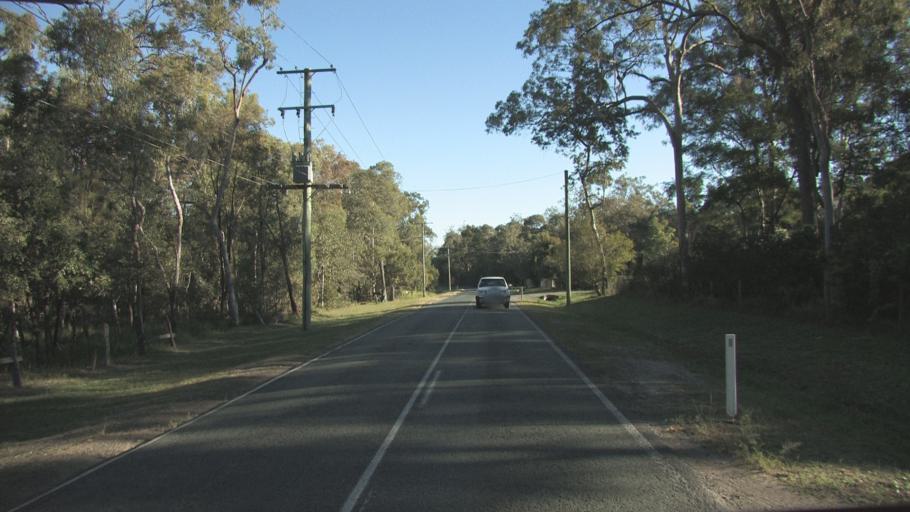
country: AU
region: Queensland
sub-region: Logan
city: Chambers Flat
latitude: -27.7539
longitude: 153.0511
